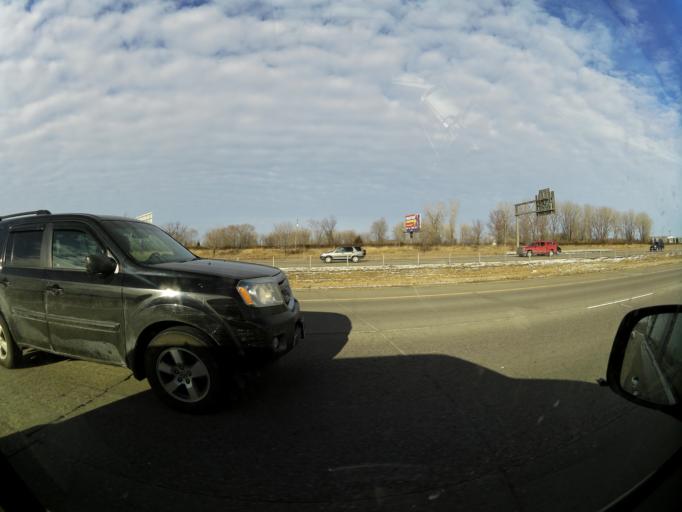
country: US
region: Minnesota
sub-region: Washington County
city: Lake Elmo
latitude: 44.9485
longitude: -92.8765
